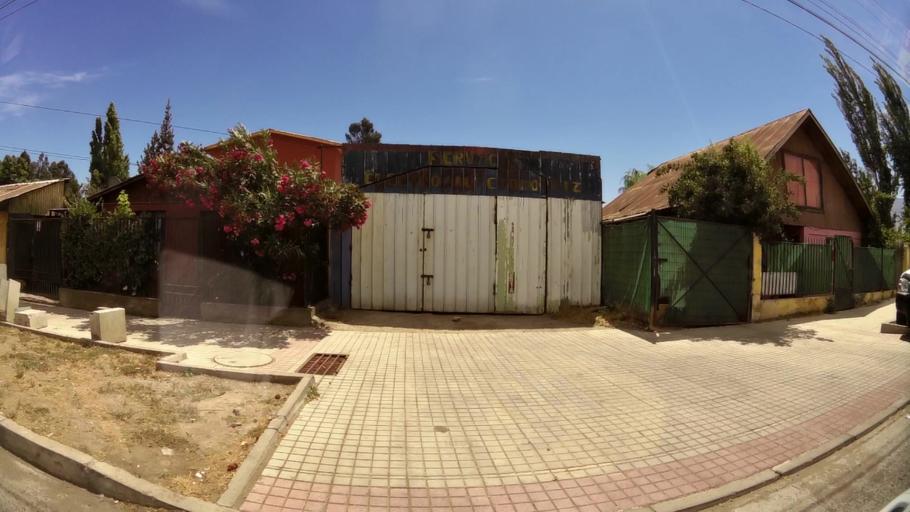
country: CL
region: O'Higgins
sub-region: Provincia de Cachapoal
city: Graneros
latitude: -33.9852
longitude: -70.7030
